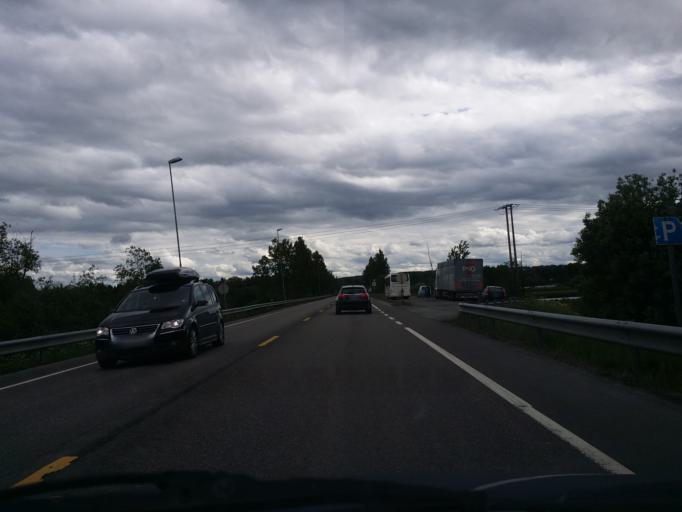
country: NO
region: Hedmark
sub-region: Hamar
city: Hamar
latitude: 60.8064
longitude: 11.1095
